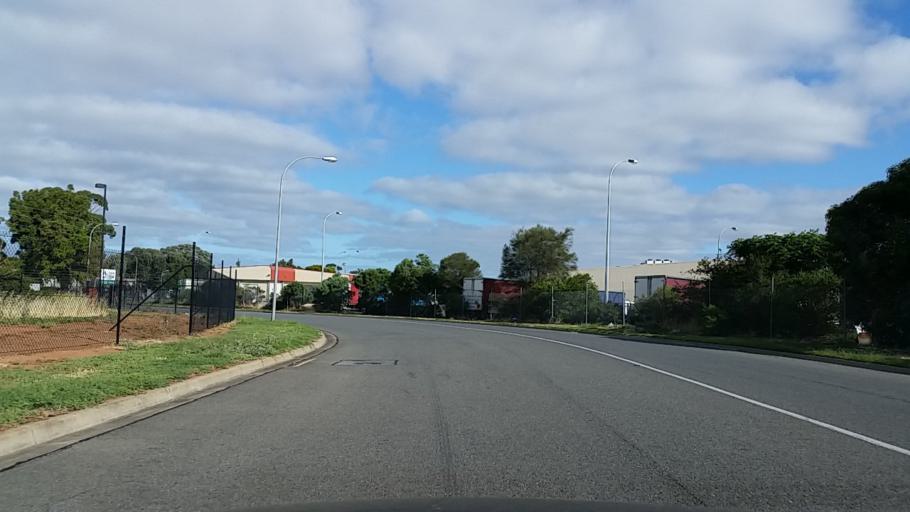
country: AU
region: South Australia
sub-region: Port Adelaide Enfield
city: Enfield
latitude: -34.8329
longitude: 138.6076
